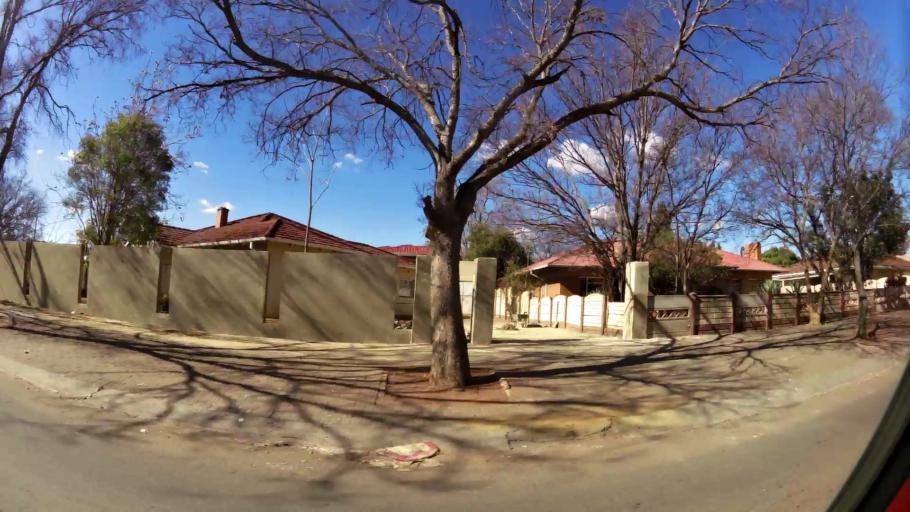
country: ZA
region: Gauteng
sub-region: West Rand District Municipality
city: Carletonville
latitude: -26.3528
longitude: 27.3926
